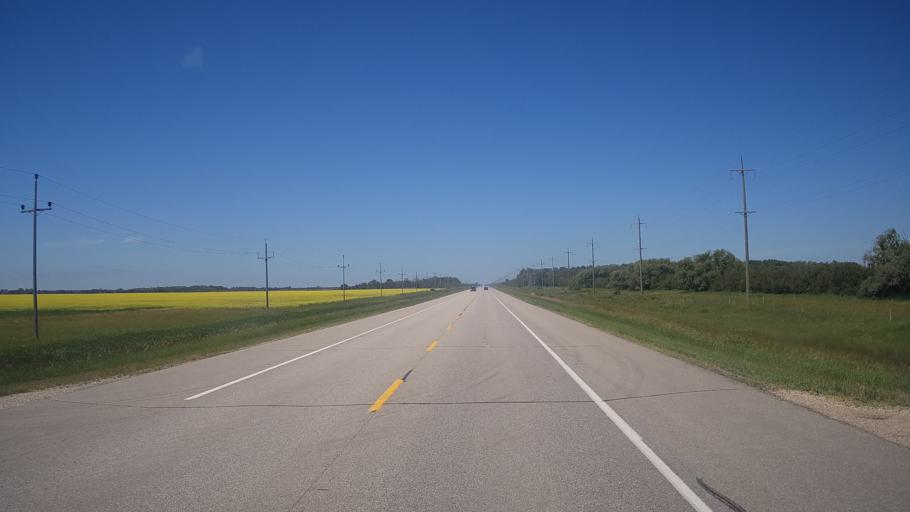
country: CA
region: Manitoba
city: Neepawa
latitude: 50.2258
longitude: -99.0881
